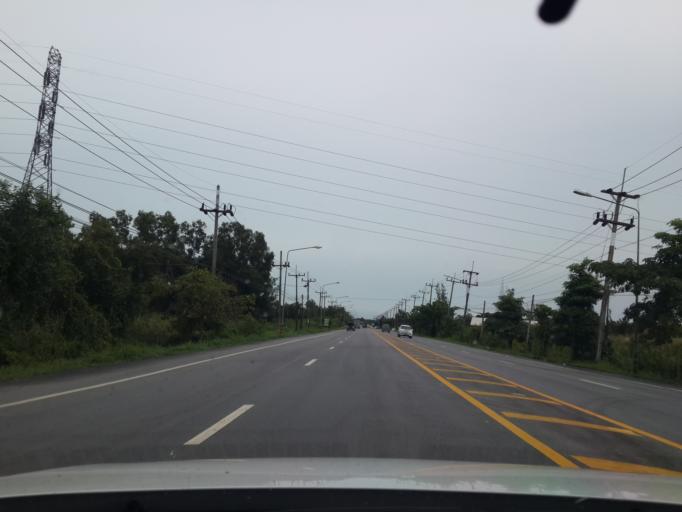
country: TH
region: Pattani
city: Nong Chik
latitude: 6.8254
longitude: 101.1632
